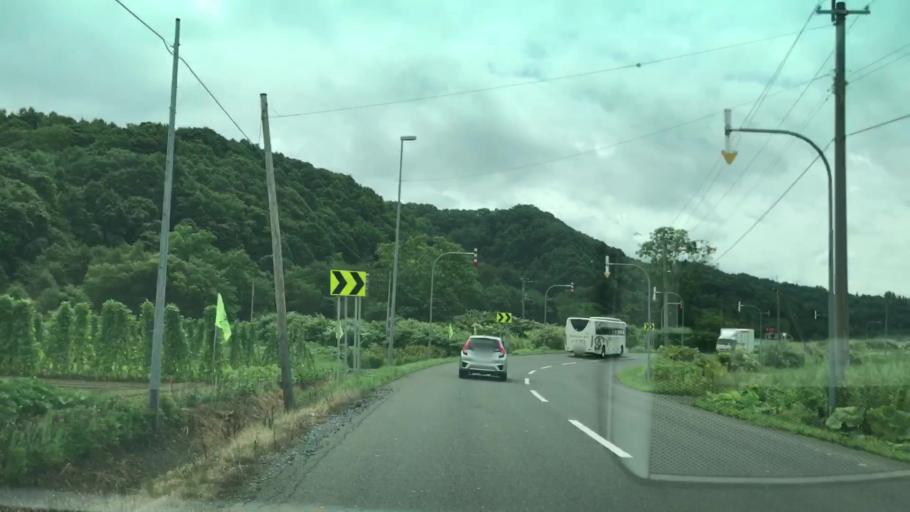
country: JP
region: Hokkaido
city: Niseko Town
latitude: 42.9465
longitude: 140.8224
